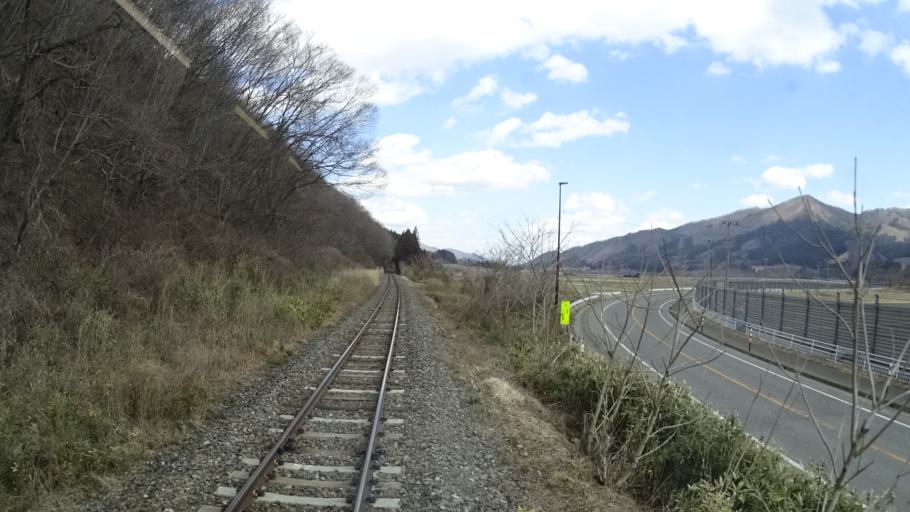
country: JP
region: Iwate
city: Tono
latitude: 39.3067
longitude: 141.4171
